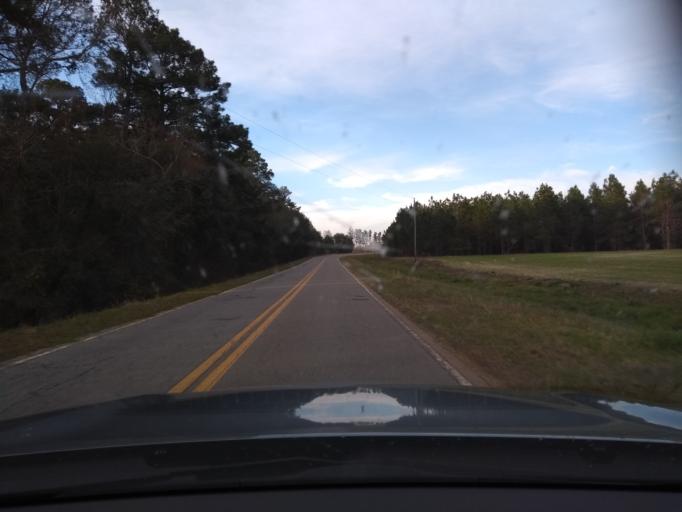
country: US
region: Georgia
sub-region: Evans County
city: Claxton
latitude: 32.2488
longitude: -81.7691
